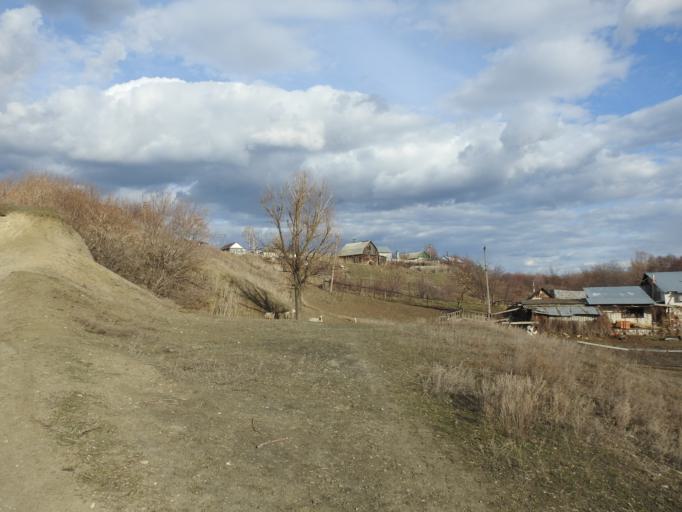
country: RU
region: Saratov
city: Sokolovyy
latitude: 51.3796
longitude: 45.8547
